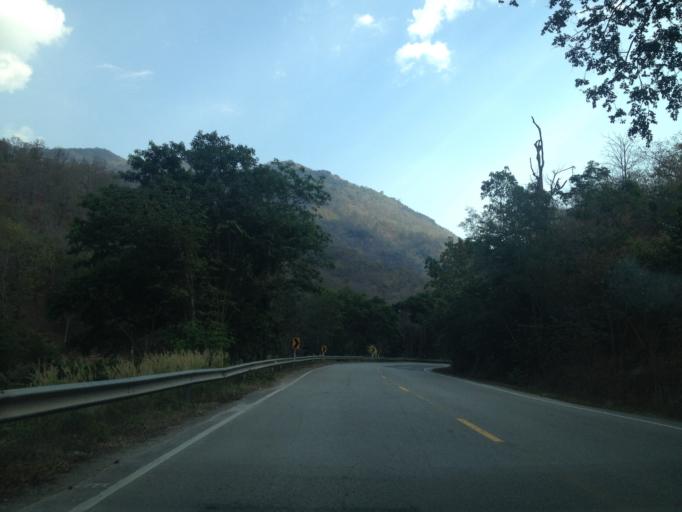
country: TH
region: Chiang Mai
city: Hot
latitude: 18.2342
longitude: 98.5446
